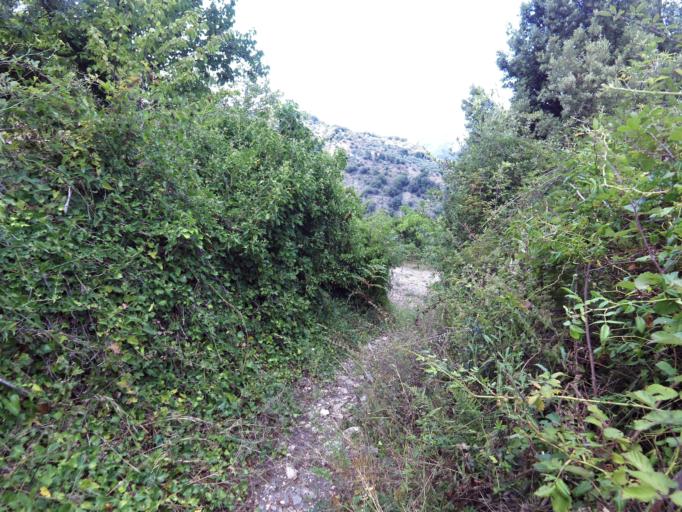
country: IT
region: Calabria
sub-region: Provincia di Reggio Calabria
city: Pazzano
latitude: 38.4724
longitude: 16.4398
